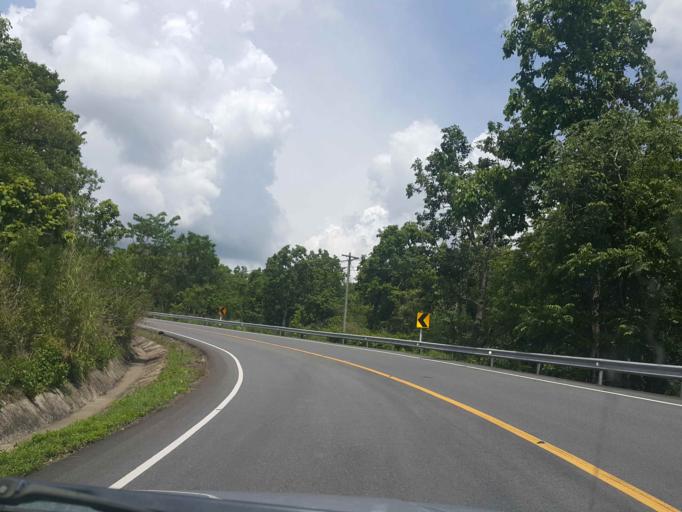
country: TH
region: Phayao
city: Chiang Muan
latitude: 18.8469
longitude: 100.3346
